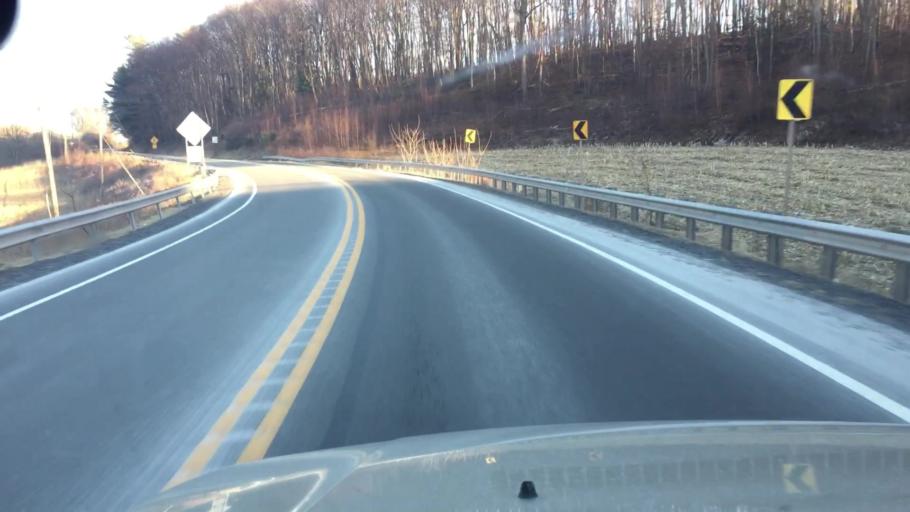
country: US
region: Pennsylvania
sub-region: Luzerne County
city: Nescopeck
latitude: 41.0536
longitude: -76.1741
